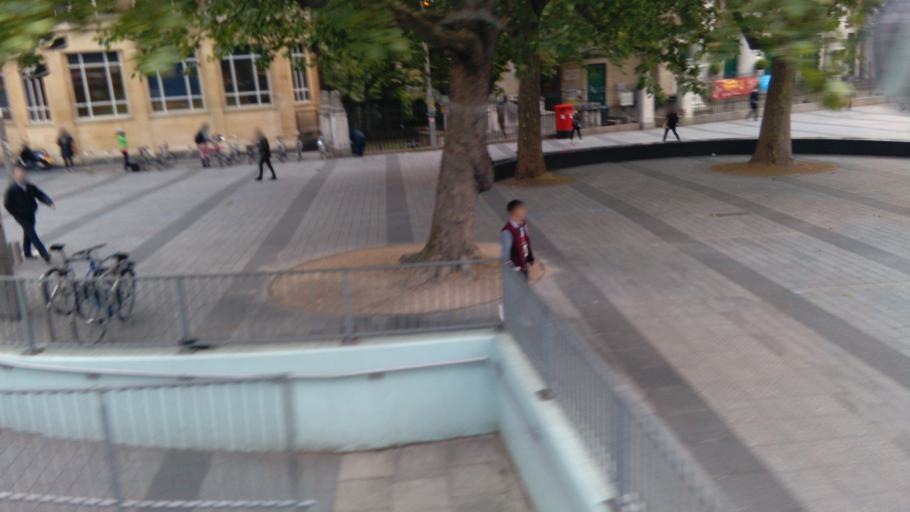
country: GB
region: England
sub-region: Greater London
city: City of Westminster
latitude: 51.5046
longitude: -0.1132
